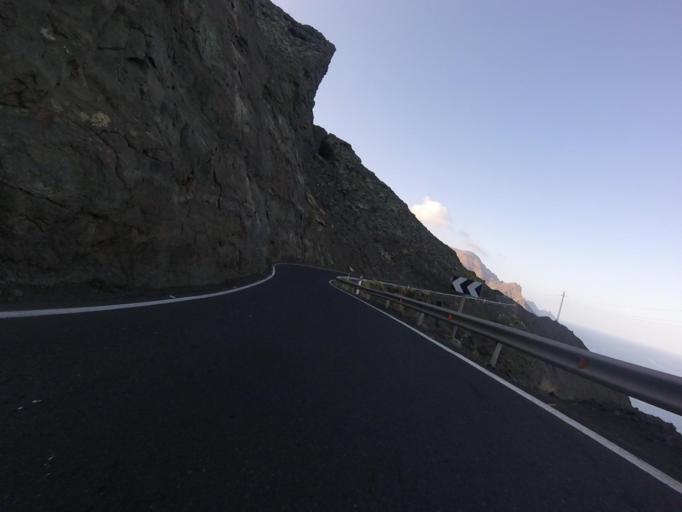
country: ES
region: Canary Islands
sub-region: Provincia de Las Palmas
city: Agaete
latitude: 28.0631
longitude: -15.7286
